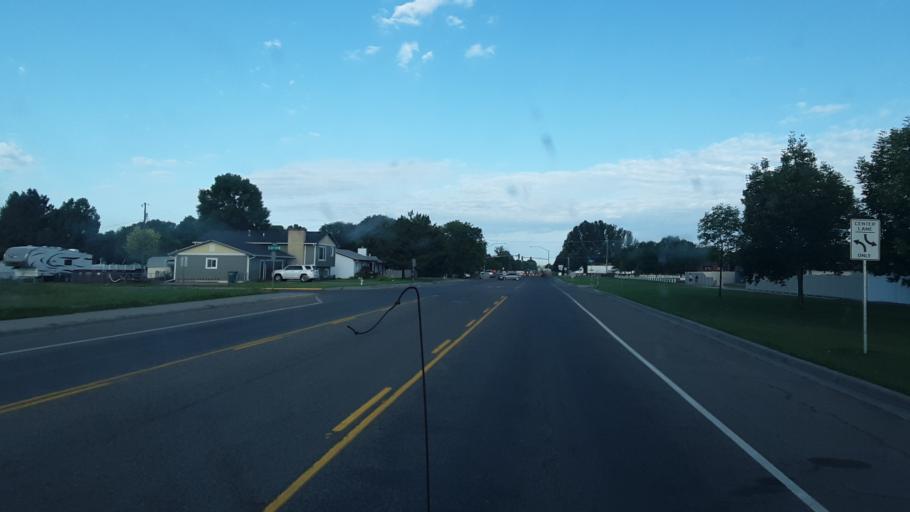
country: US
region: Montana
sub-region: Yellowstone County
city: Billings
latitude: 45.7624
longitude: -108.5934
